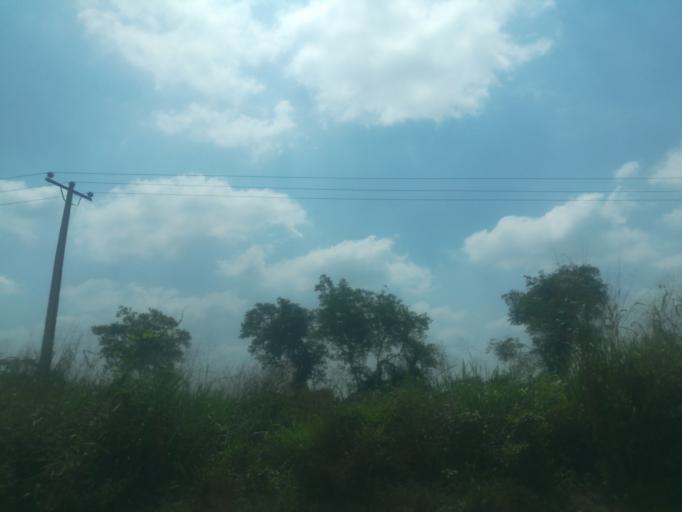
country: NG
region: Ogun
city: Abeokuta
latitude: 7.1398
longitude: 3.4075
